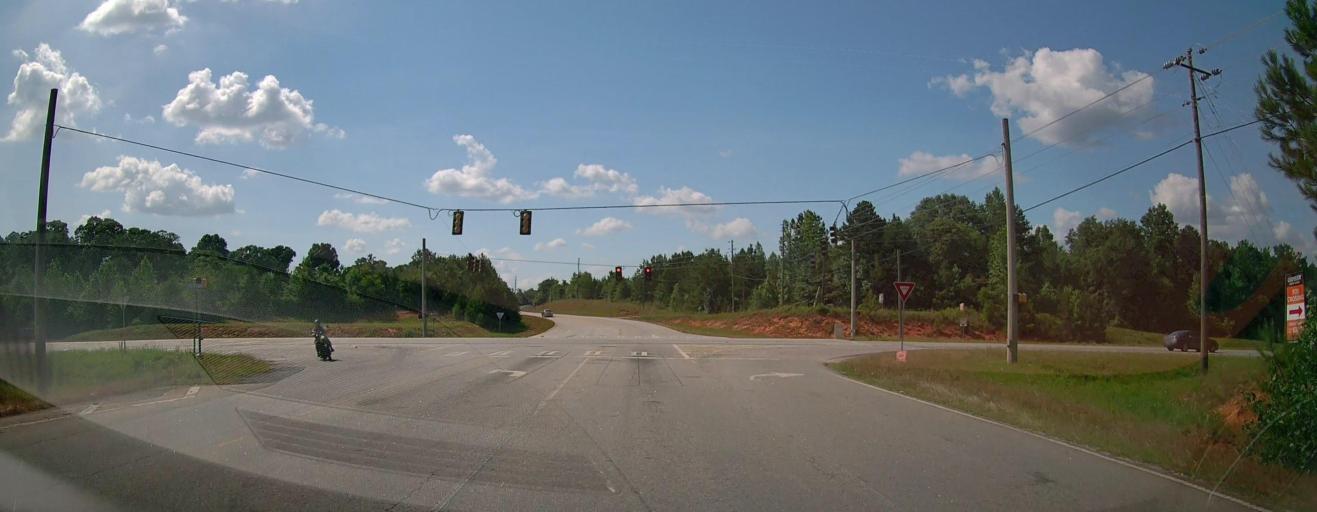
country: US
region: Georgia
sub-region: Spalding County
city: East Griffin
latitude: 33.2397
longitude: -84.1645
